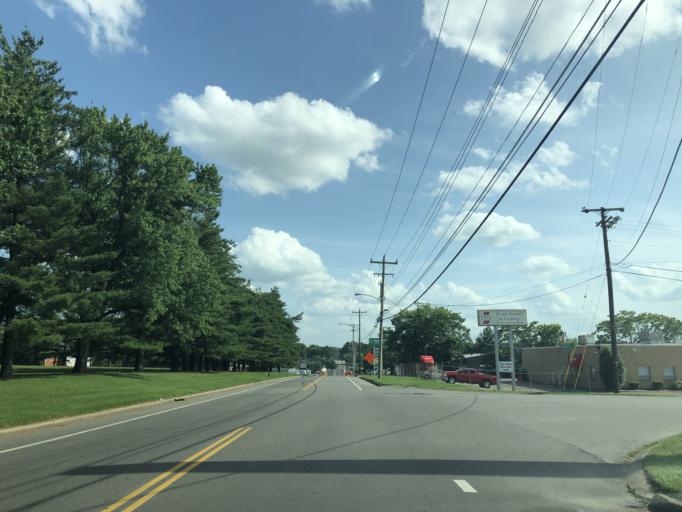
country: US
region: Tennessee
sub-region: Davidson County
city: Nashville
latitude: 36.1302
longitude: -86.7418
